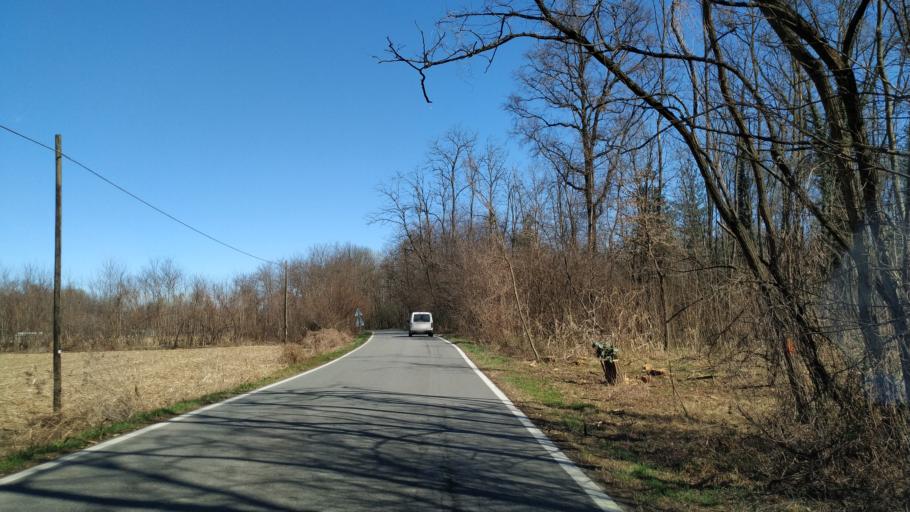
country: IT
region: Piedmont
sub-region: Provincia di Novara
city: Ghemme
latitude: 45.5825
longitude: 8.4083
